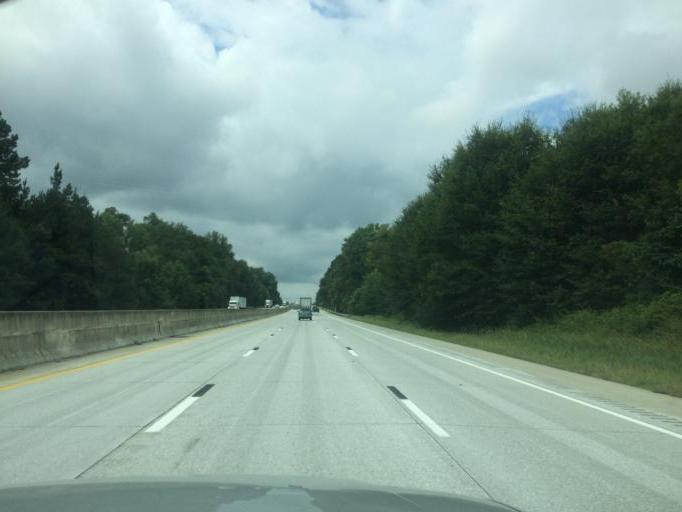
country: US
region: South Carolina
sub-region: Anderson County
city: Williamston
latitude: 34.6494
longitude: -82.5726
